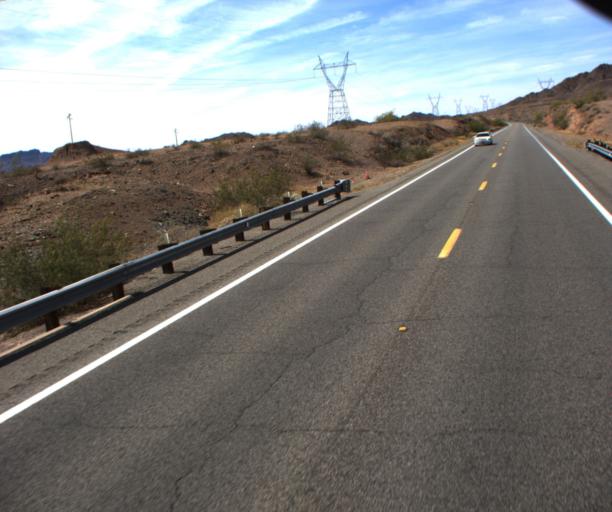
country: US
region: Arizona
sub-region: La Paz County
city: Cienega Springs
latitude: 34.3339
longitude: -114.1371
